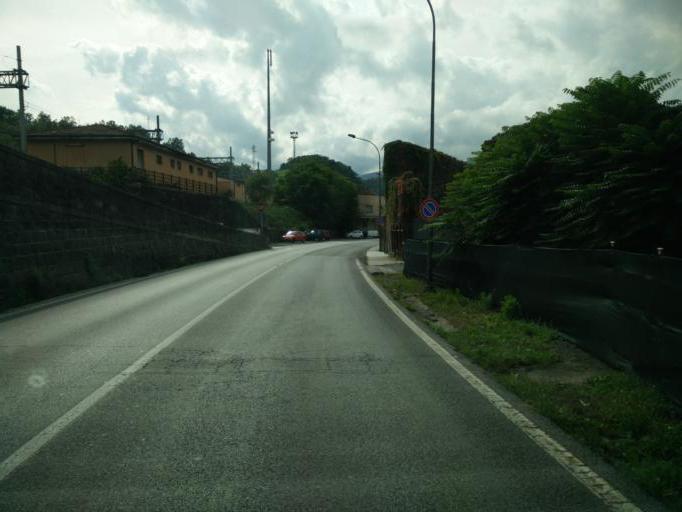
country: IT
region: Tuscany
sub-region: Provincia di Massa-Carrara
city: Pontremoli
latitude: 44.3716
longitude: 9.8872
